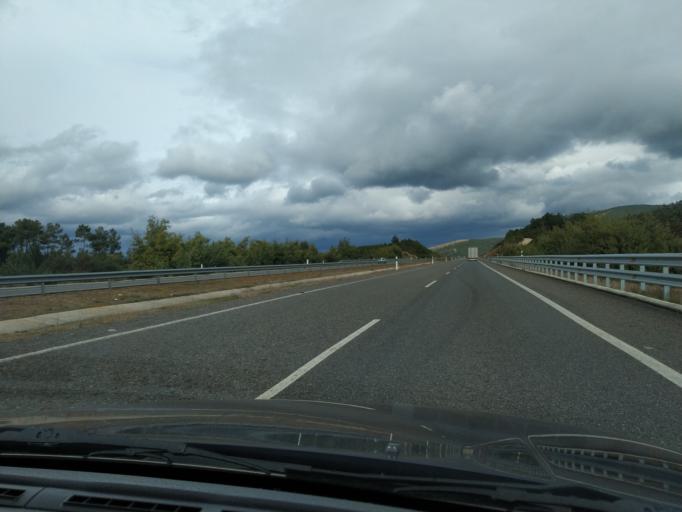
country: ES
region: Galicia
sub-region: Provincia de Ourense
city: Oimbra
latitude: 41.8807
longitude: -7.4286
